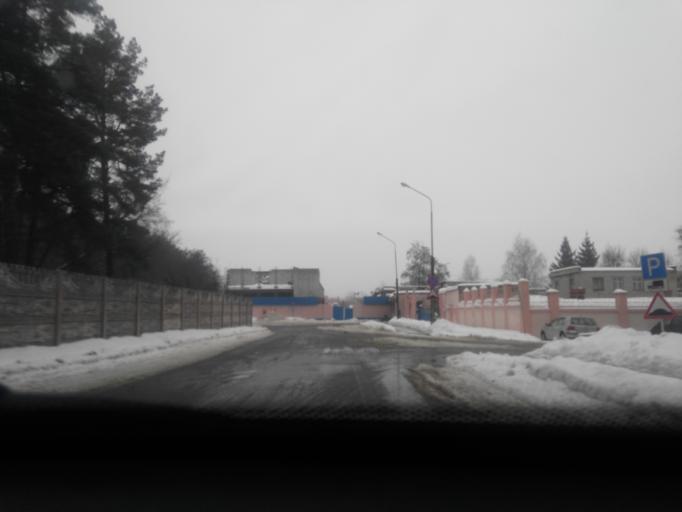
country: BY
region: Mogilev
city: Babruysk
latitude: 53.1679
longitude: 29.2079
